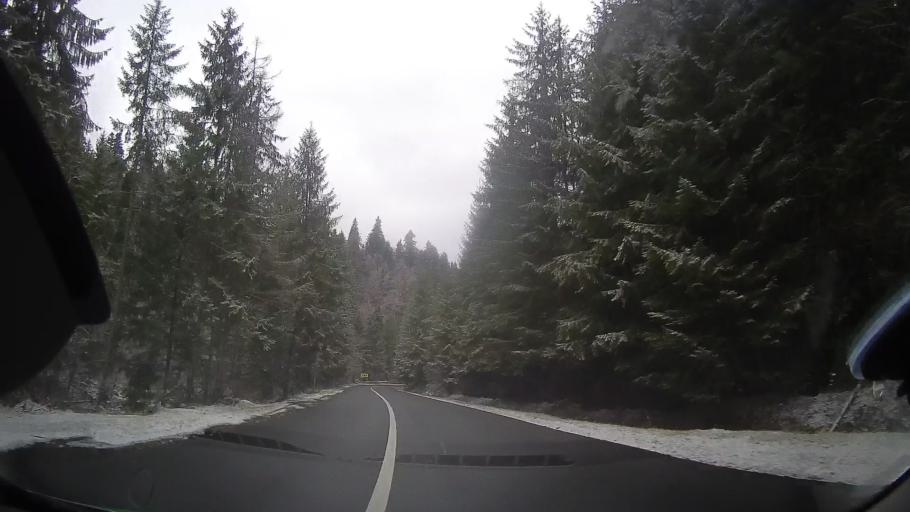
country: RO
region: Cluj
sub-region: Comuna Calatele
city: Calatele
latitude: 46.7334
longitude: 23.0398
